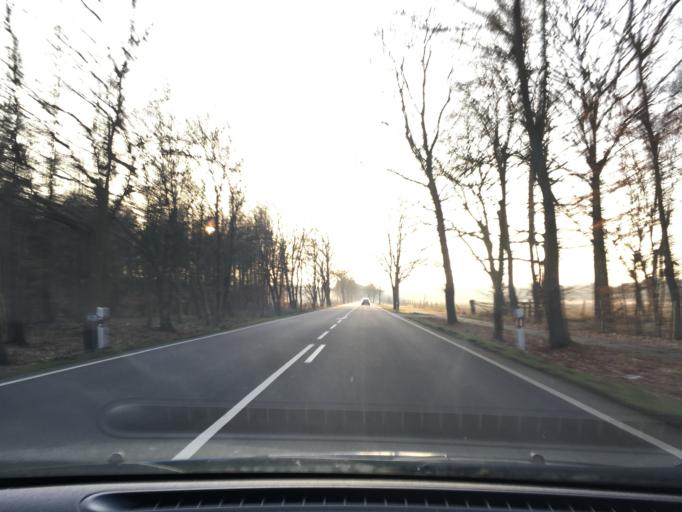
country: DE
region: Lower Saxony
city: Sprakensehl
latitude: 52.7967
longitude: 10.3973
